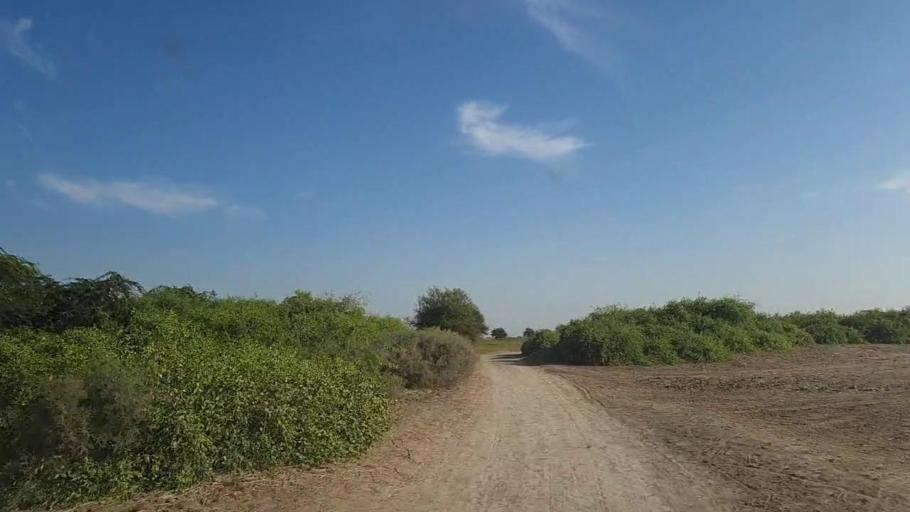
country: PK
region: Sindh
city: Mirpur Batoro
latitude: 24.7571
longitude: 68.3641
